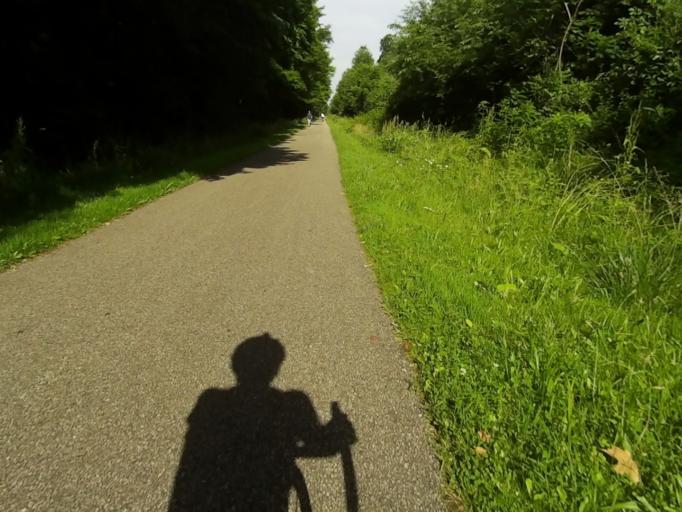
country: US
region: Ohio
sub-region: Summit County
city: Stow
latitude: 41.1913
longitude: -81.4043
